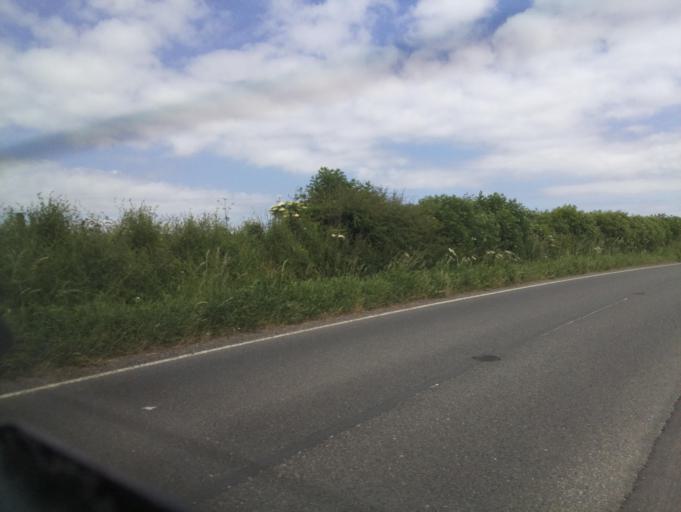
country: GB
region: England
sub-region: Dorset
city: Sherborne
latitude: 50.9823
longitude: -2.5106
